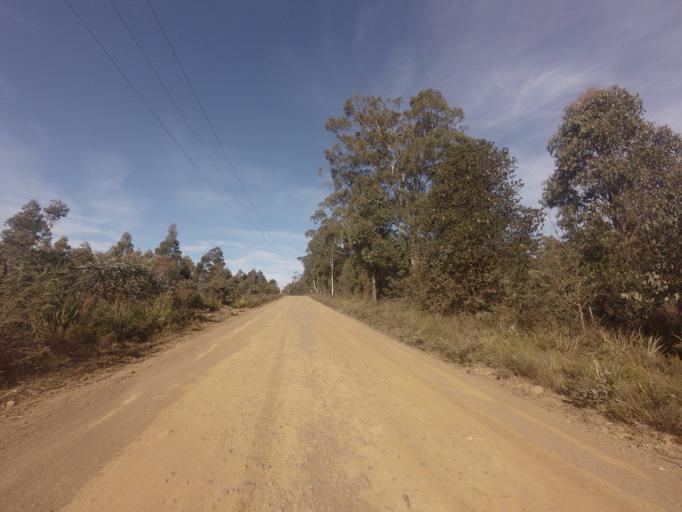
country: AU
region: Tasmania
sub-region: Sorell
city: Sorell
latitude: -42.4982
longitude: 147.5310
